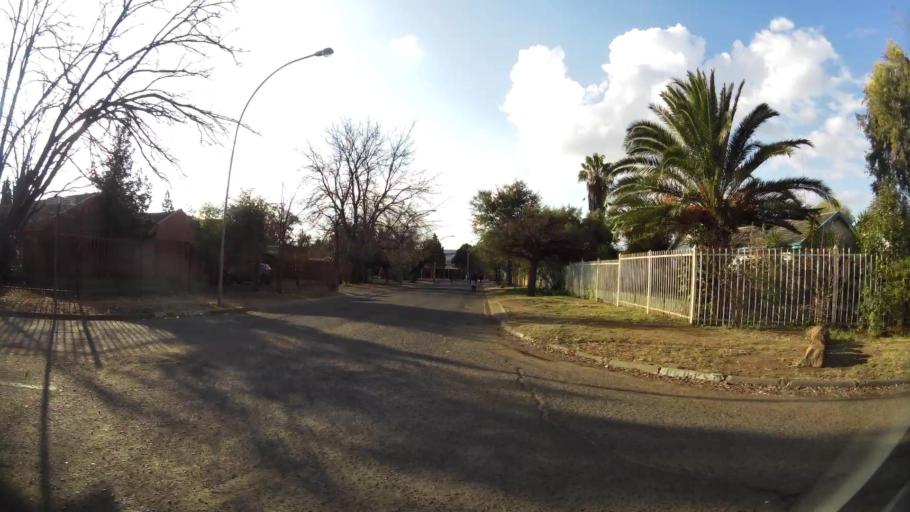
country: ZA
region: Orange Free State
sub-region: Mangaung Metropolitan Municipality
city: Bloemfontein
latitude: -29.1502
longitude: 26.1768
